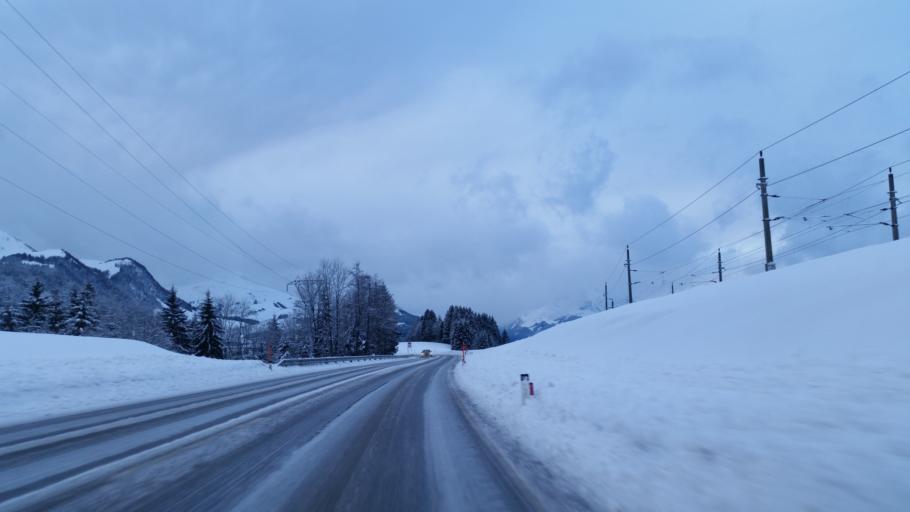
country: AT
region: Tyrol
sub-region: Politischer Bezirk Kitzbuhel
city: Fieberbrunn
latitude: 47.4683
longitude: 12.5725
